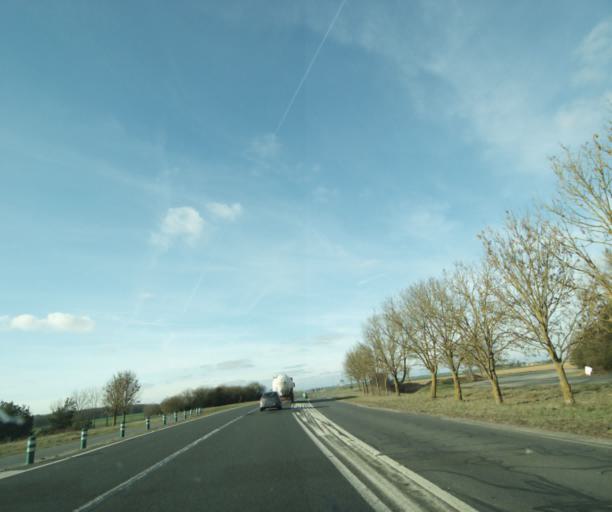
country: FR
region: Ile-de-France
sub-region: Departement des Yvelines
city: Ablis
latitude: 48.4799
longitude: 1.8497
